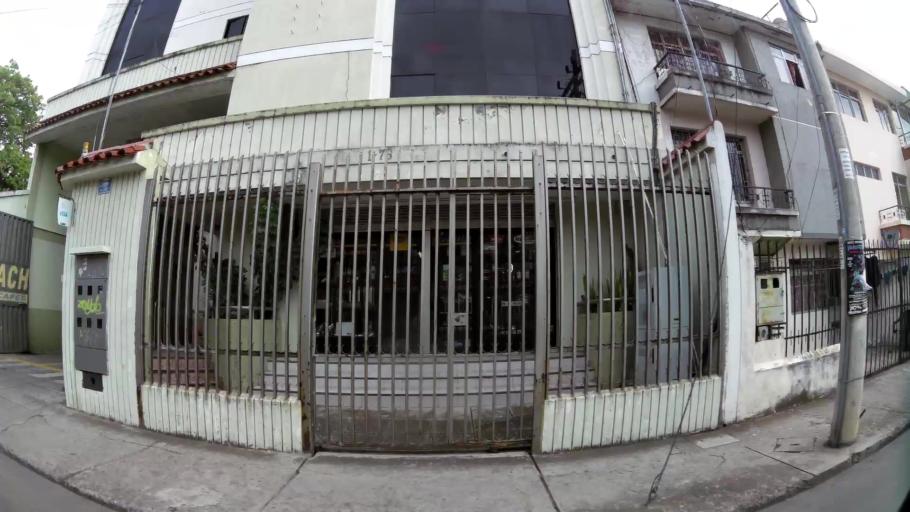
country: EC
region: Azuay
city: Cuenca
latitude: -2.9060
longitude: -78.9956
